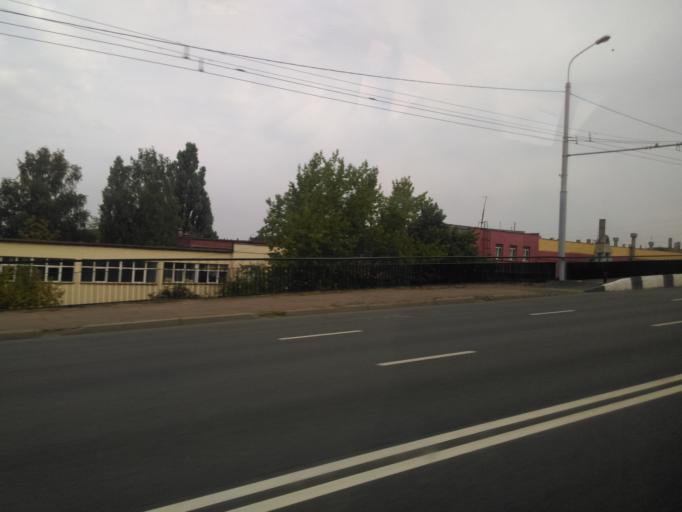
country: BY
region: Minsk
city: Minsk
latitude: 53.8912
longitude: 27.6358
